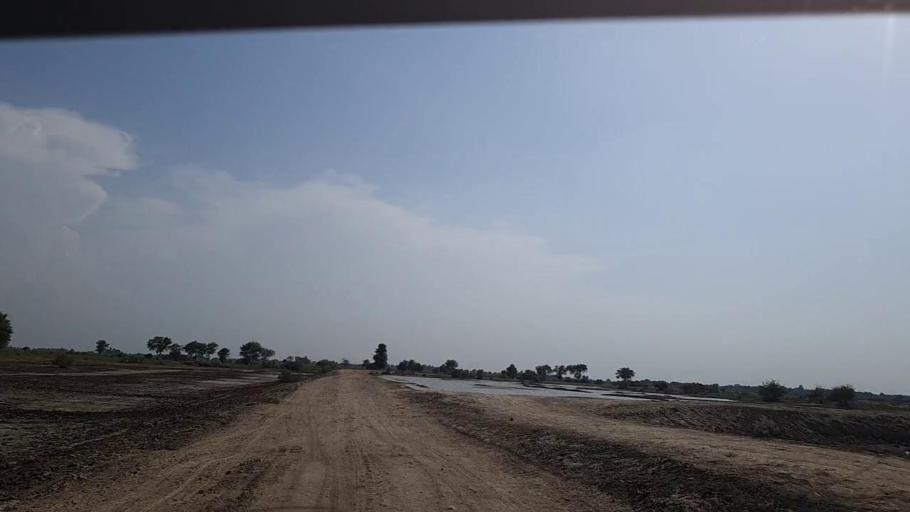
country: PK
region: Sindh
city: Khanpur
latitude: 27.8382
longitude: 69.3266
